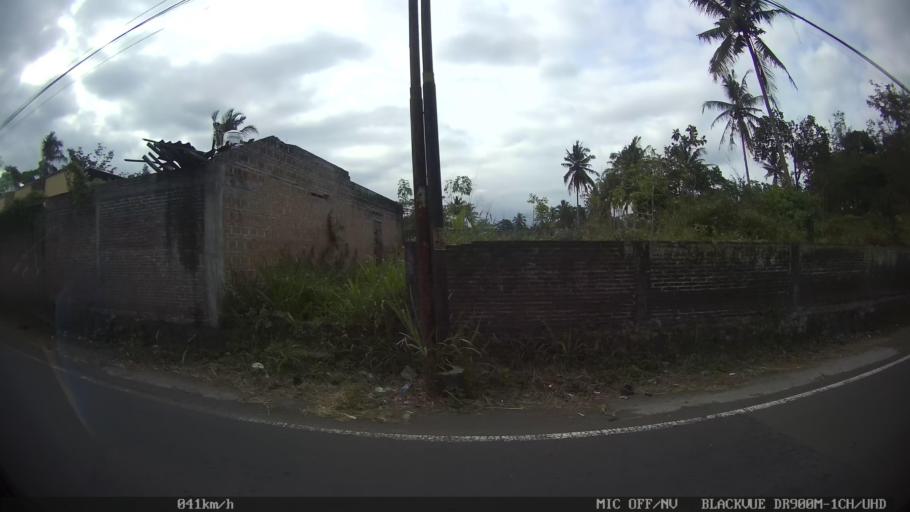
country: ID
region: Daerah Istimewa Yogyakarta
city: Depok
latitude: -7.6829
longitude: 110.4383
